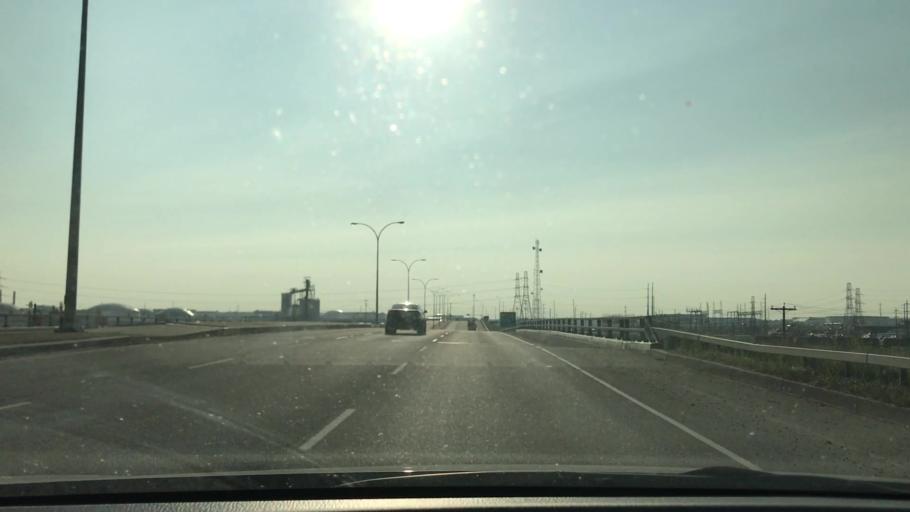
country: CA
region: Alberta
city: Sherwood Park
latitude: 53.5410
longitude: -113.3805
